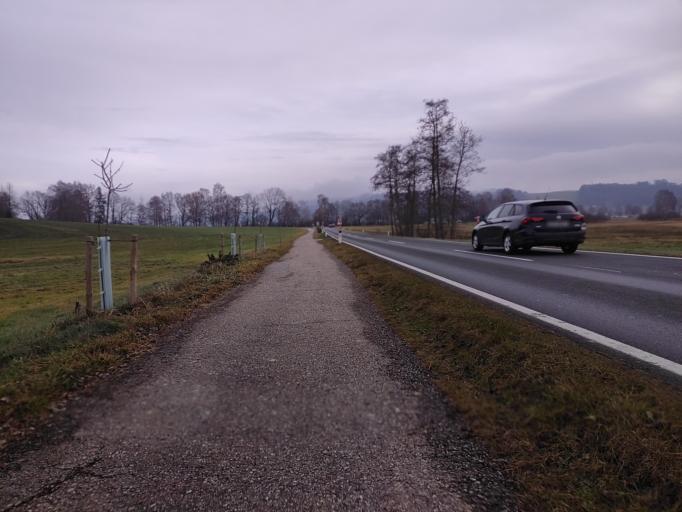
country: AT
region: Salzburg
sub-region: Politischer Bezirk Salzburg-Umgebung
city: Mattsee
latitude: 47.9836
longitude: 13.1002
